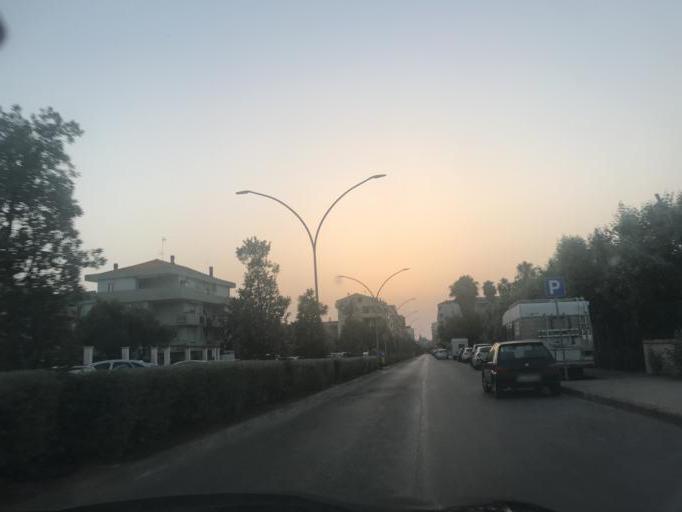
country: IT
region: Sardinia
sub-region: Provincia di Sassari
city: Alghero
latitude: 40.5521
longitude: 8.3257
